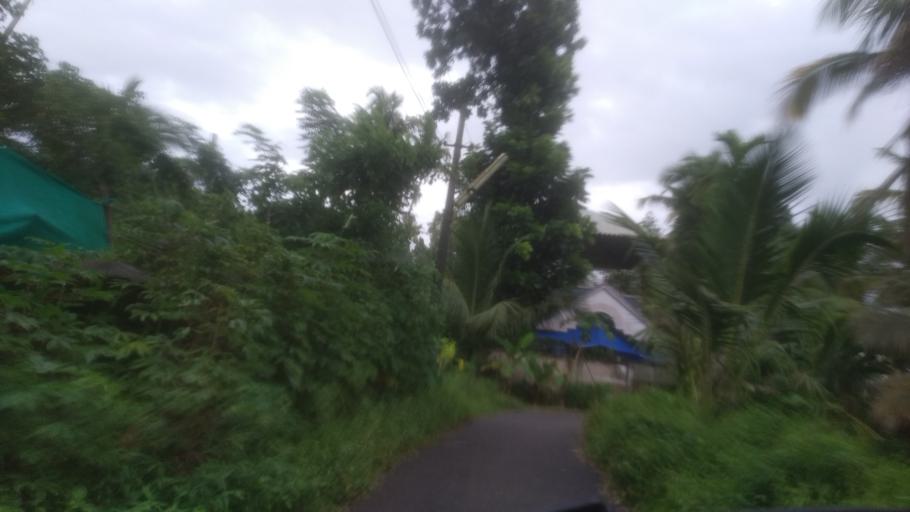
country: IN
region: Kerala
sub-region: Ernakulam
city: Elur
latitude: 10.0815
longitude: 76.2057
